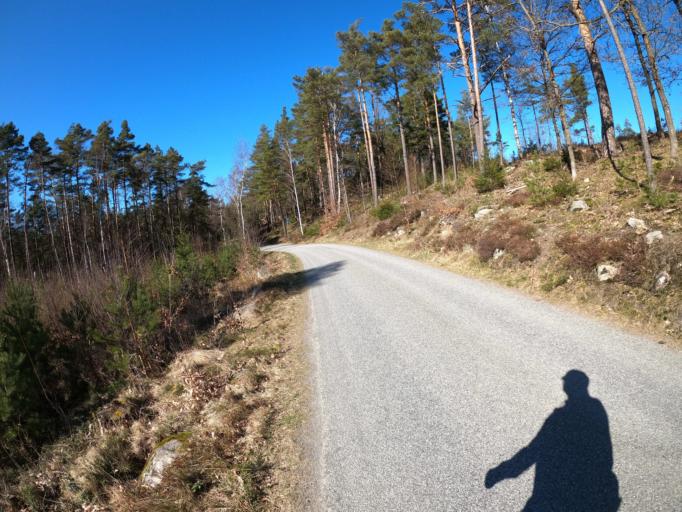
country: SE
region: Vaestra Goetaland
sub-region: Harryda Kommun
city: Molnlycke
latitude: 57.6319
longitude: 12.1200
